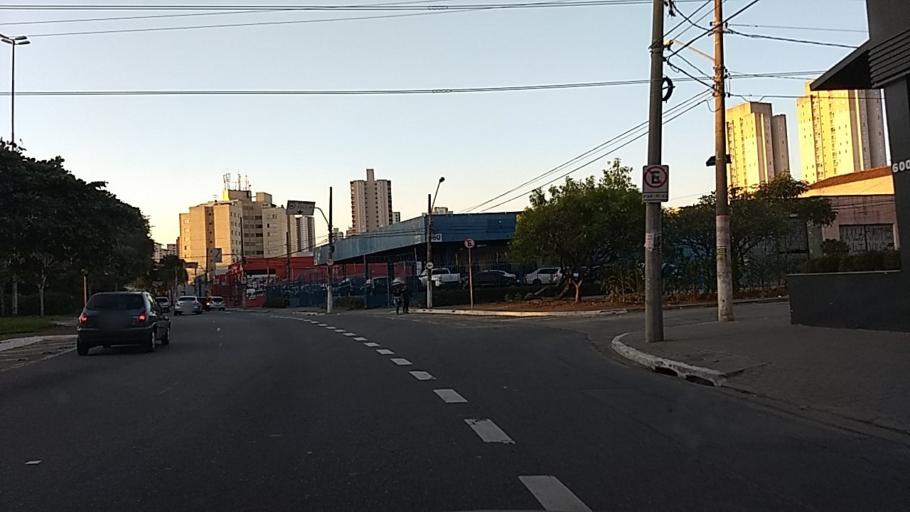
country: BR
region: Sao Paulo
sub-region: Sao Paulo
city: Sao Paulo
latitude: -23.5113
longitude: -46.6058
